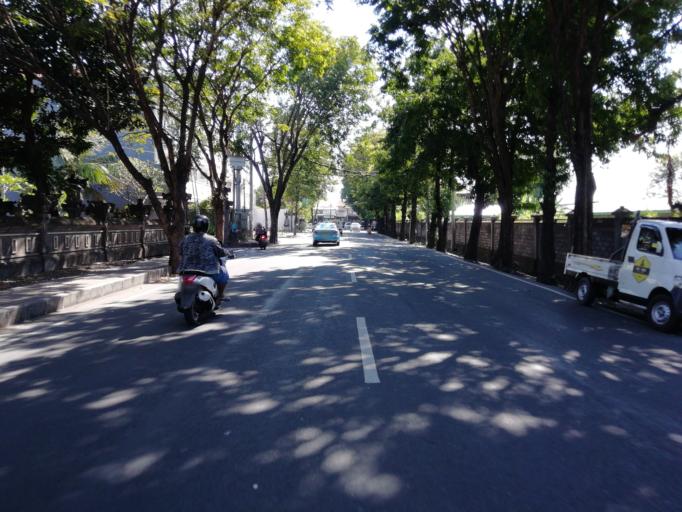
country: ID
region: Bali
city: Karyadharma
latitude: -8.7109
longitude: 115.2173
